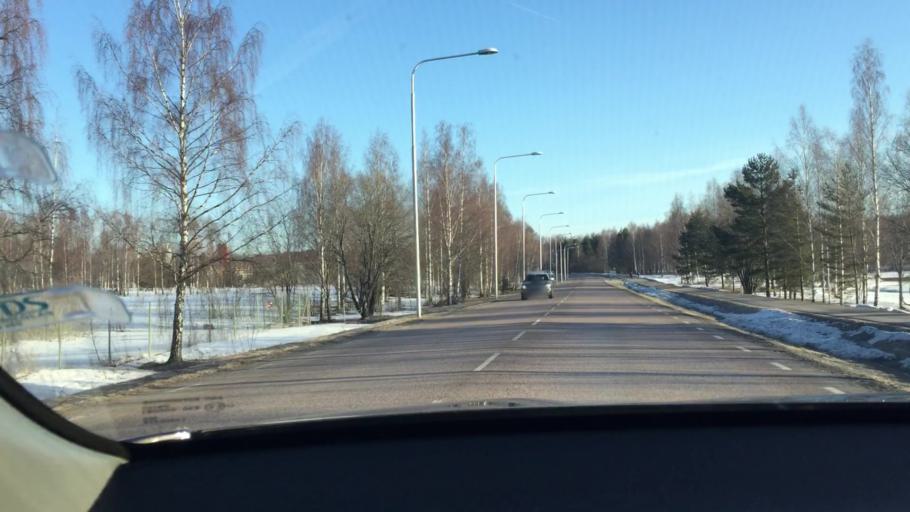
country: SE
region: Dalarna
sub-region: Faluns Kommun
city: Falun
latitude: 60.5827
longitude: 15.6536
